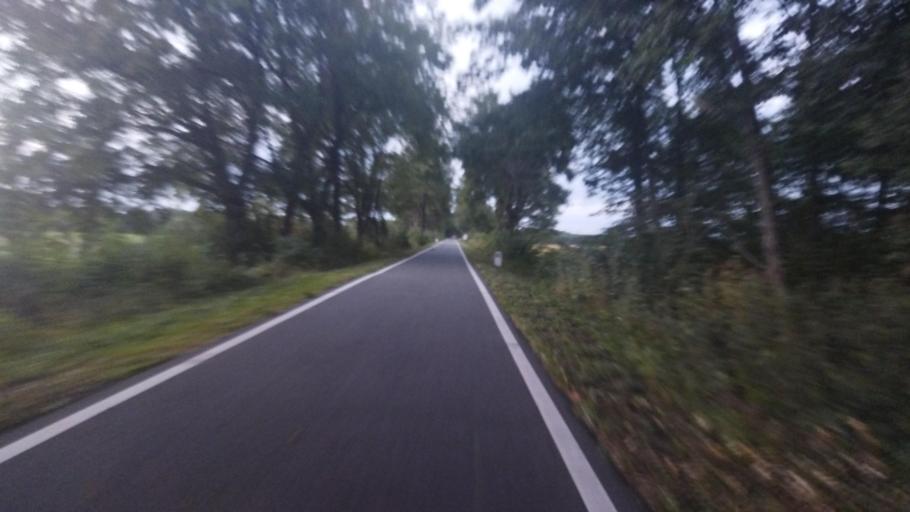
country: DE
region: North Rhine-Westphalia
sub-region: Regierungsbezirk Munster
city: Horstmar
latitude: 52.0907
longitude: 7.3266
